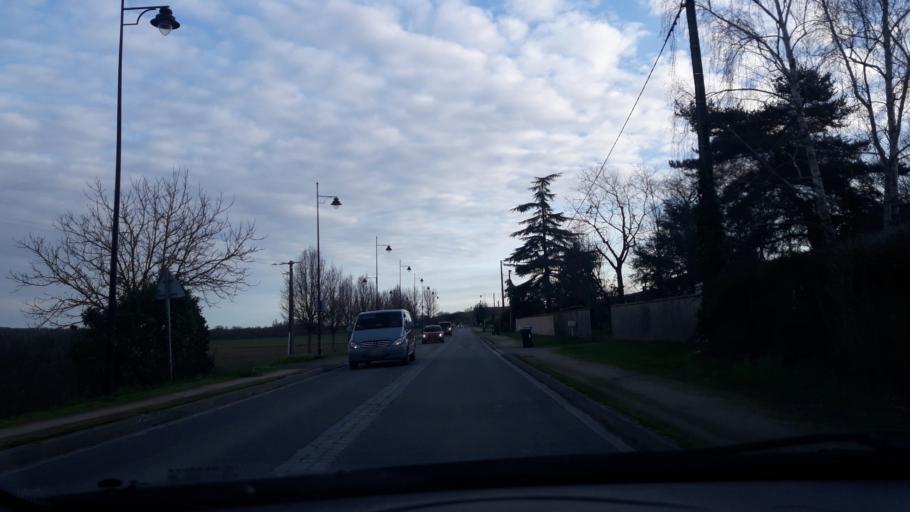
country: FR
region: Midi-Pyrenees
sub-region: Departement de la Haute-Garonne
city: Levignac
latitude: 43.6696
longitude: 1.1985
